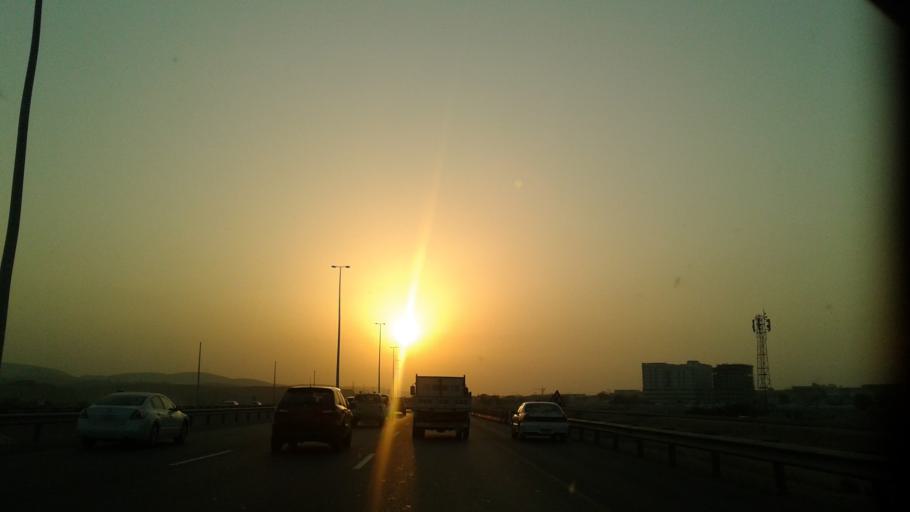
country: OM
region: Muhafazat Masqat
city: Bawshar
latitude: 23.5646
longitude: 58.3548
